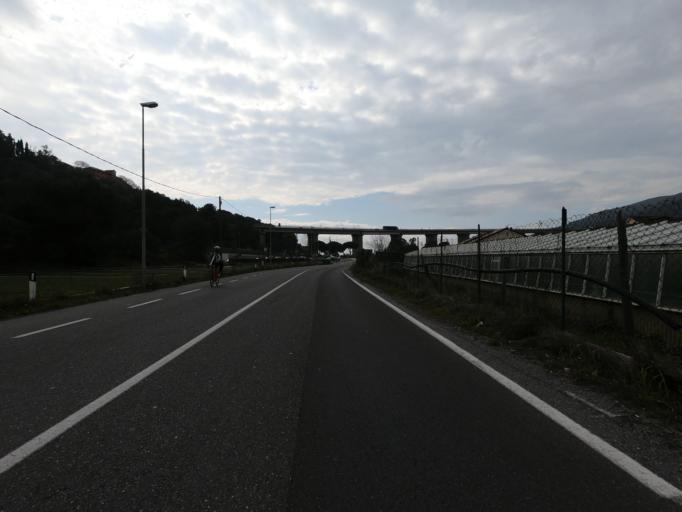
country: IT
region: Liguria
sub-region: Provincia di Savona
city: Andora
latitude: 43.9677
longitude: 8.1413
